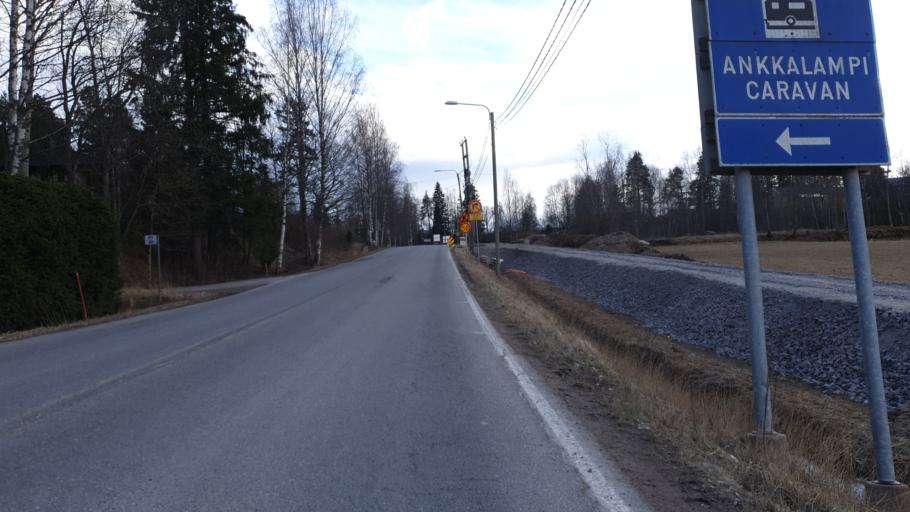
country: FI
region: Uusimaa
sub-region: Helsinki
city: Nurmijaervi
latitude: 60.3513
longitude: 24.8625
